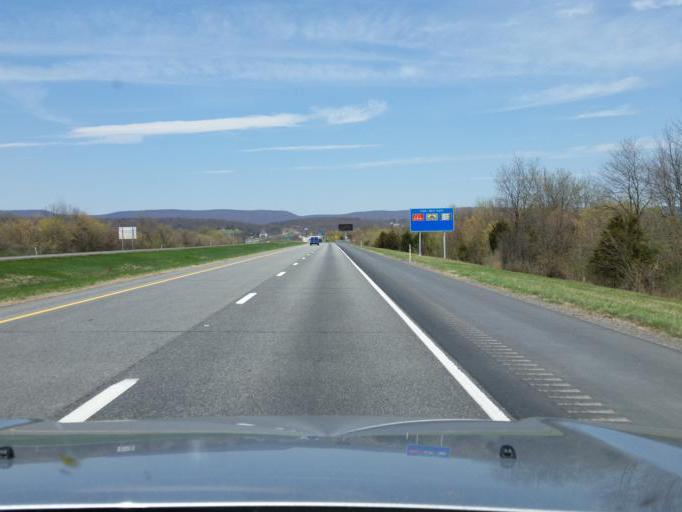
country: US
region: Pennsylvania
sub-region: Juniata County
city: Mifflintown
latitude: 40.5693
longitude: -77.3666
